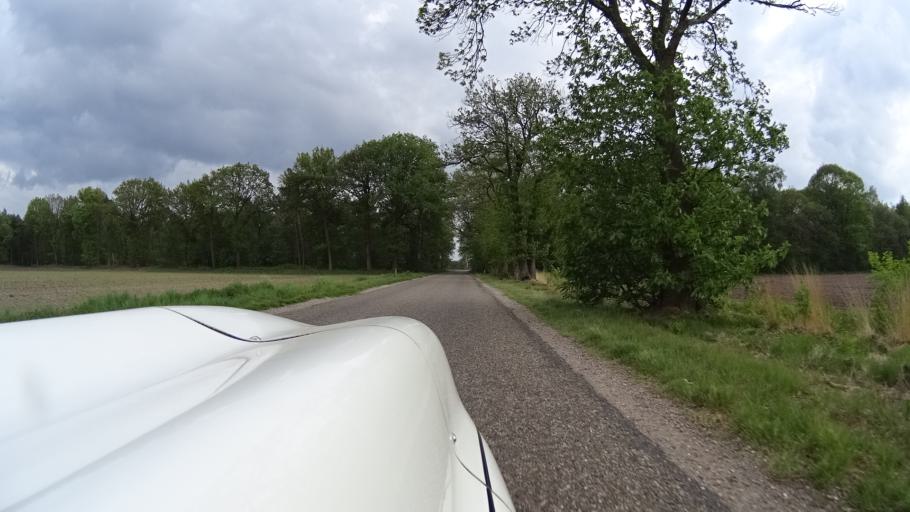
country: NL
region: North Brabant
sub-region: Gemeente Uden
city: Odiliapeel
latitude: 51.6323
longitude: 5.7072
